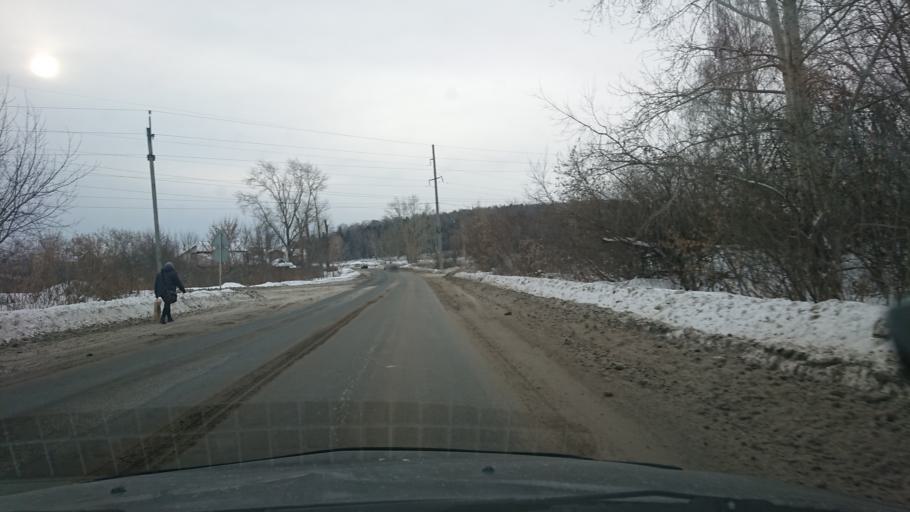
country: RU
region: Sverdlovsk
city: Istok
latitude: 56.7787
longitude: 60.7402
